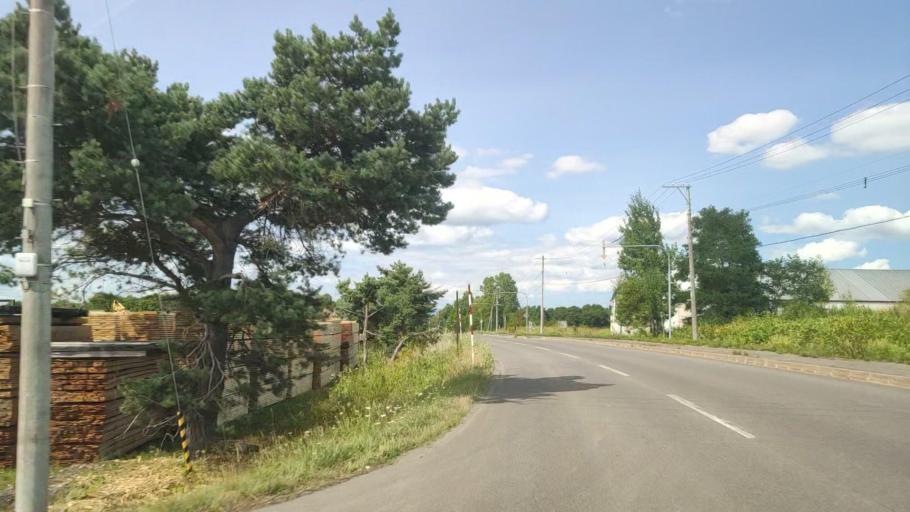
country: JP
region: Hokkaido
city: Nayoro
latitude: 44.2838
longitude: 142.4294
